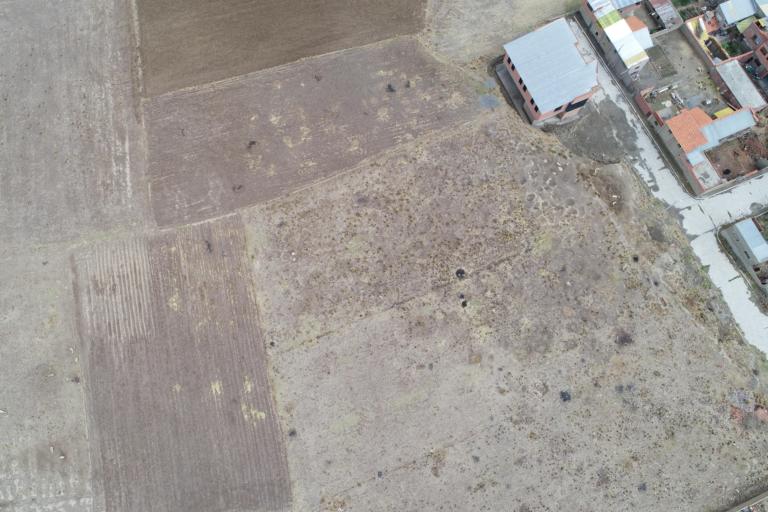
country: BO
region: La Paz
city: Achacachi
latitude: -16.0331
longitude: -68.6906
